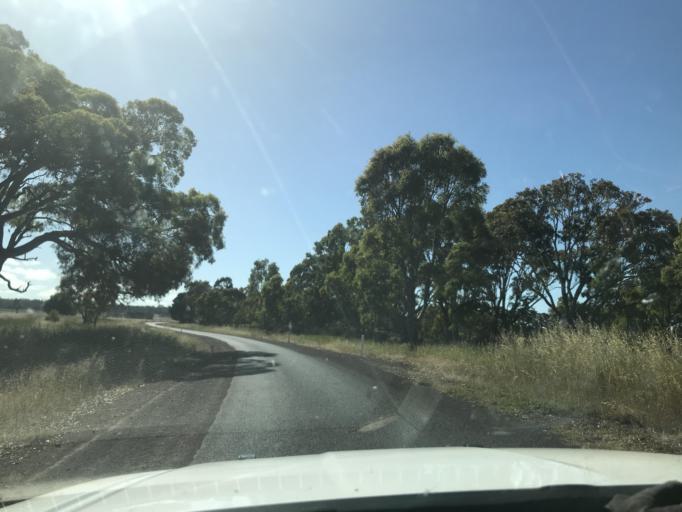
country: AU
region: Victoria
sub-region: Horsham
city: Horsham
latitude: -37.0875
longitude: 141.7576
